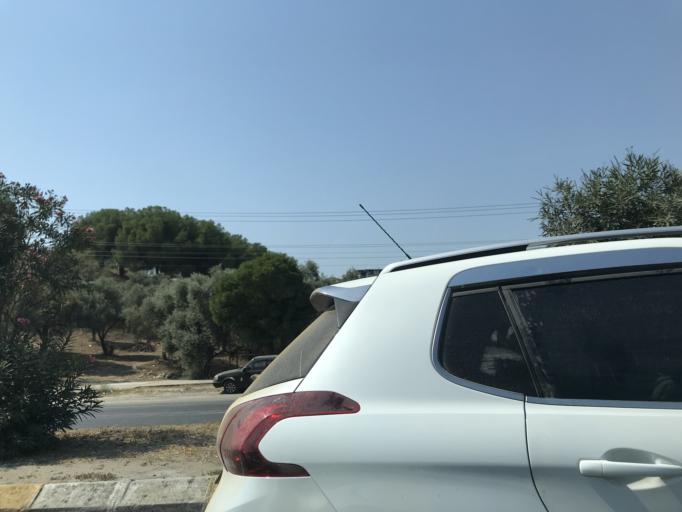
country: TR
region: Mugla
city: Milas
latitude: 37.3182
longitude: 27.7897
